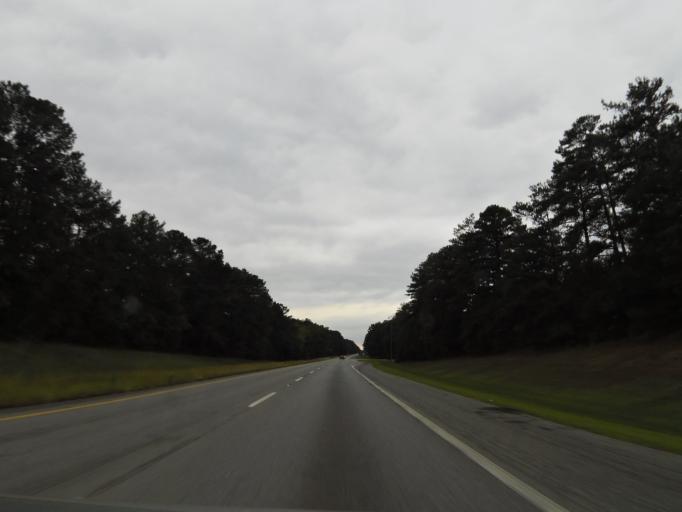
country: US
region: Alabama
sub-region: Saint Clair County
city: Ashville
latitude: 33.8760
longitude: -86.2667
